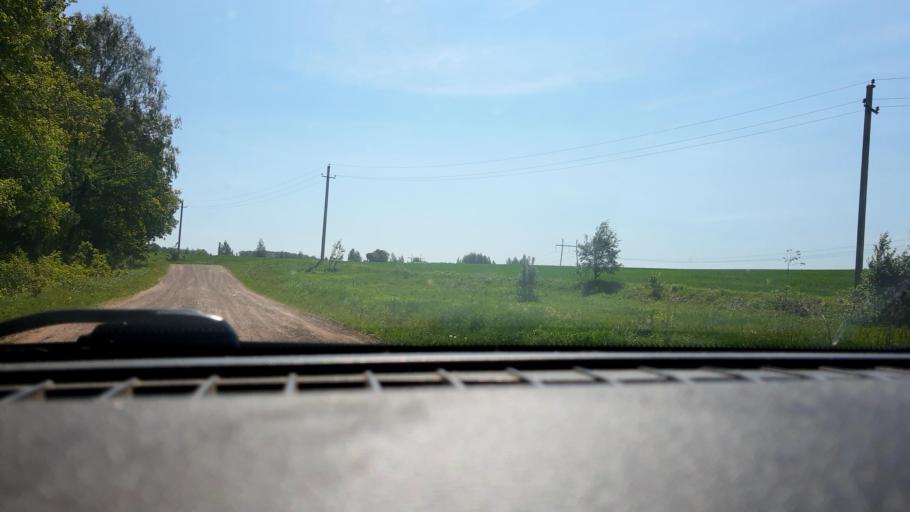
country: RU
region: Bashkortostan
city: Avdon
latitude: 54.4271
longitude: 55.8419
